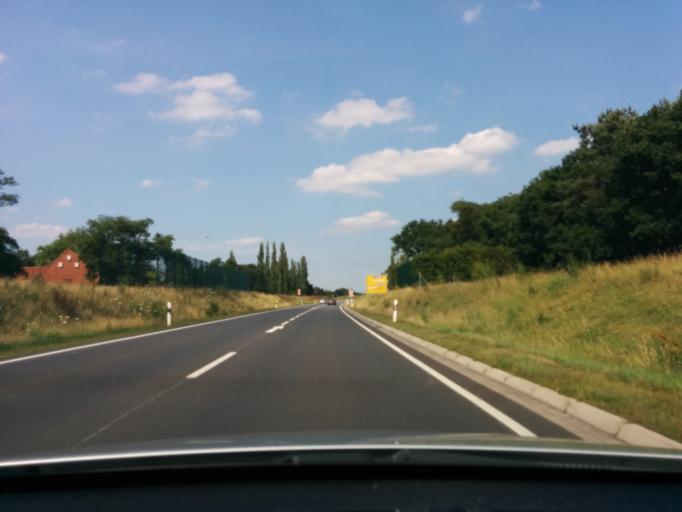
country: DE
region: North Rhine-Westphalia
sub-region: Regierungsbezirk Munster
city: Neuenkirchen
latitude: 52.2210
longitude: 7.3720
